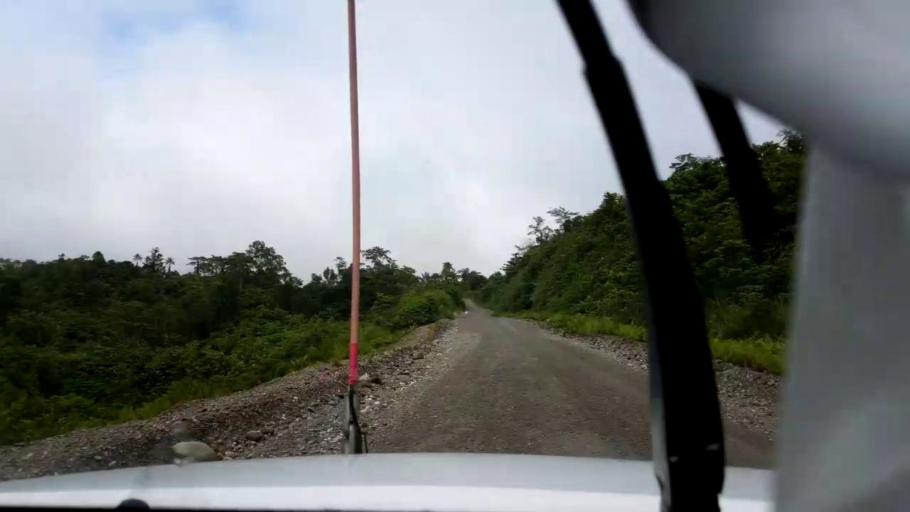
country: PG
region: Western Province
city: Kiunga
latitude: -5.5222
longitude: 141.2807
